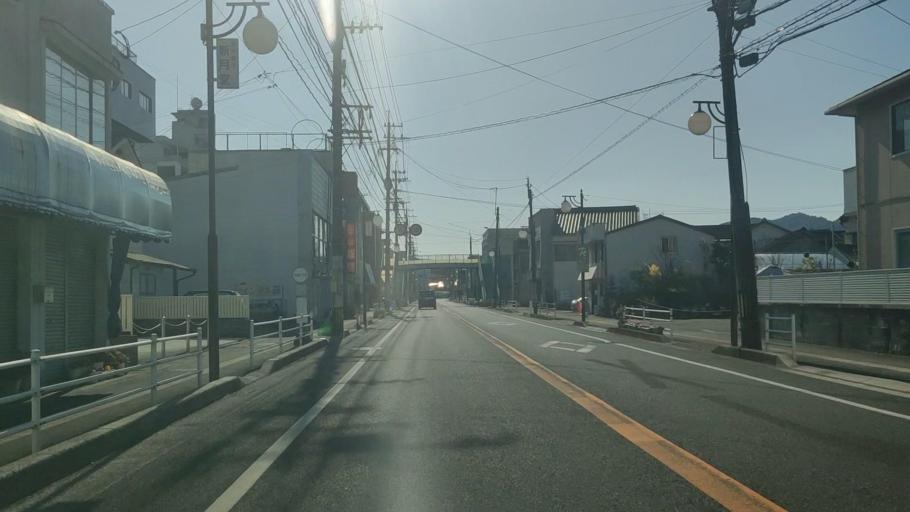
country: JP
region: Oita
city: Saiki
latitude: 32.9644
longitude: 131.9007
